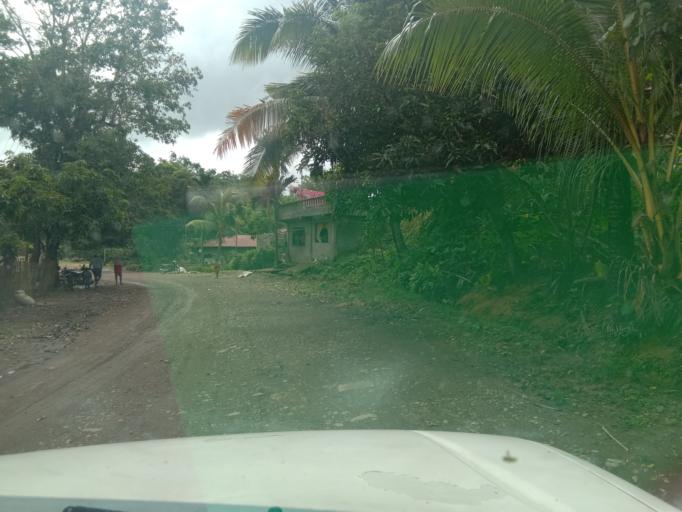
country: PH
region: Western Visayas
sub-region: Province of Capiz
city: Lantangan
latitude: 11.3631
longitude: 122.9069
